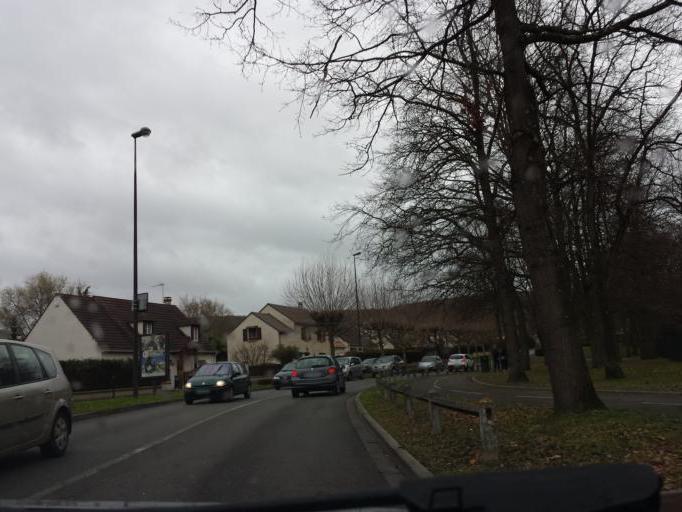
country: FR
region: Ile-de-France
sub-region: Departement du Val-d'Oise
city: Montigny-les-Cormeilles
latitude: 48.9908
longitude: 2.2156
